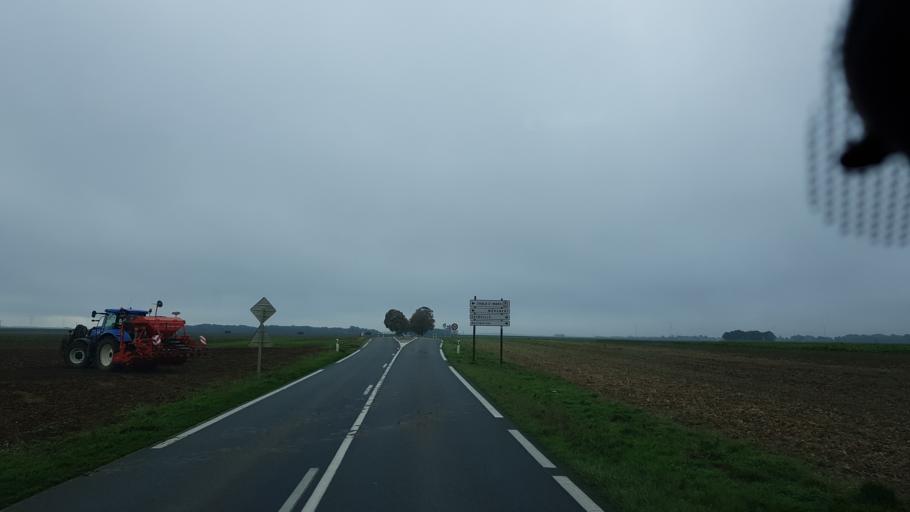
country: FR
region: Ile-de-France
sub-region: Departement de l'Essonne
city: Pussay
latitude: 48.4159
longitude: 1.9659
